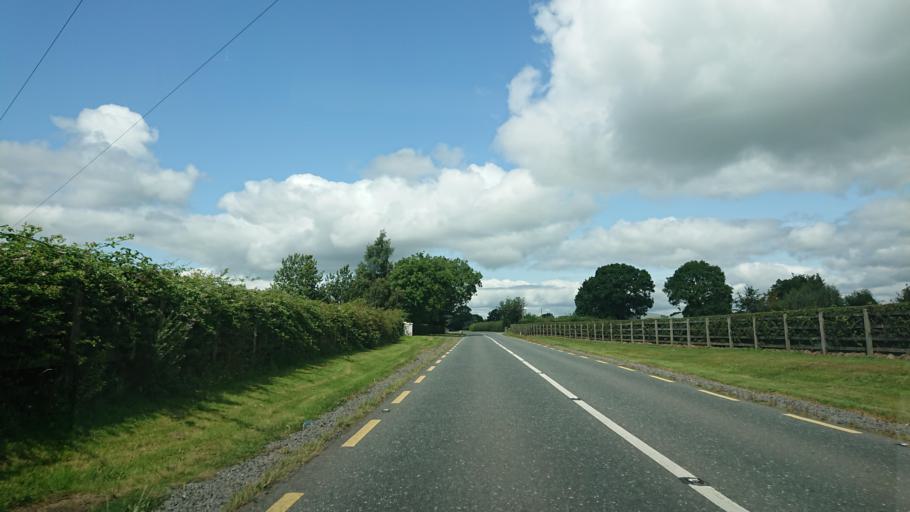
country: IE
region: Leinster
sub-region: Kildare
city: Kilcock
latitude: 53.3787
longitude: -6.7034
